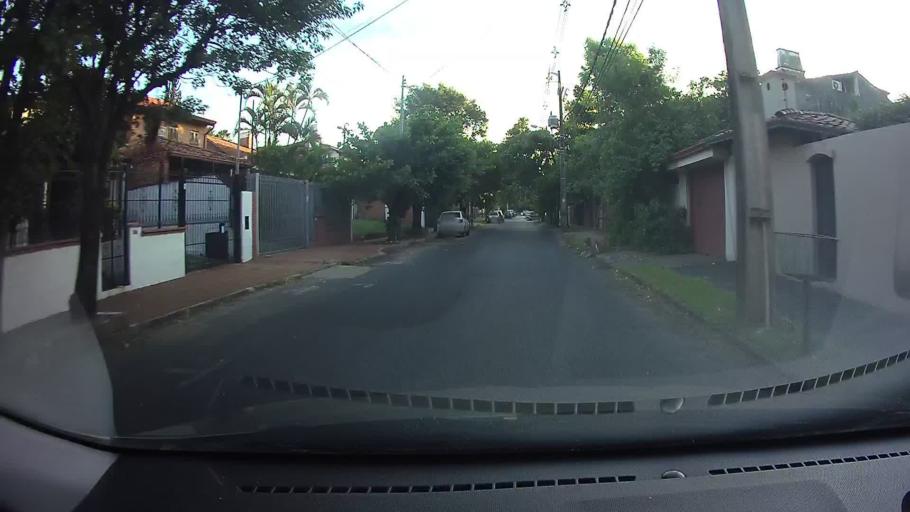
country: PY
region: Central
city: Lambare
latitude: -25.3026
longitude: -57.5754
